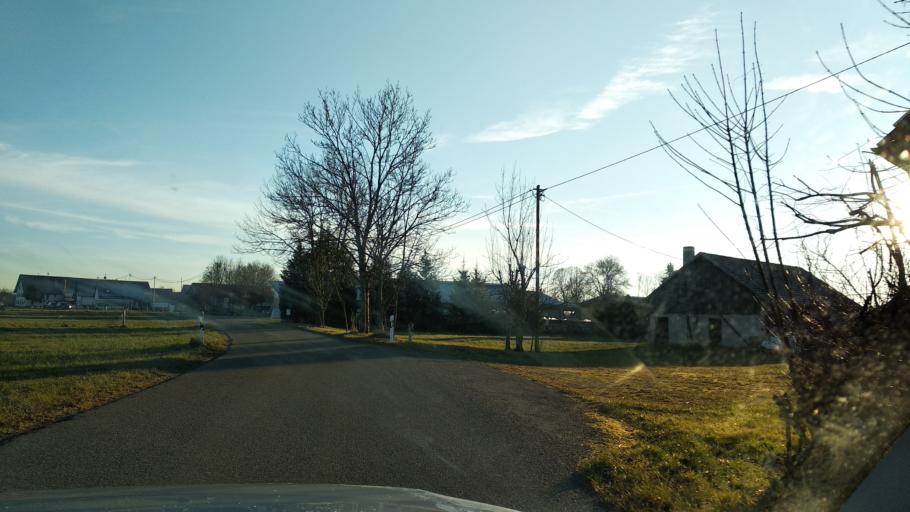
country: DE
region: Bavaria
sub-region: Swabia
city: Lautrach
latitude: 47.9159
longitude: 10.1299
